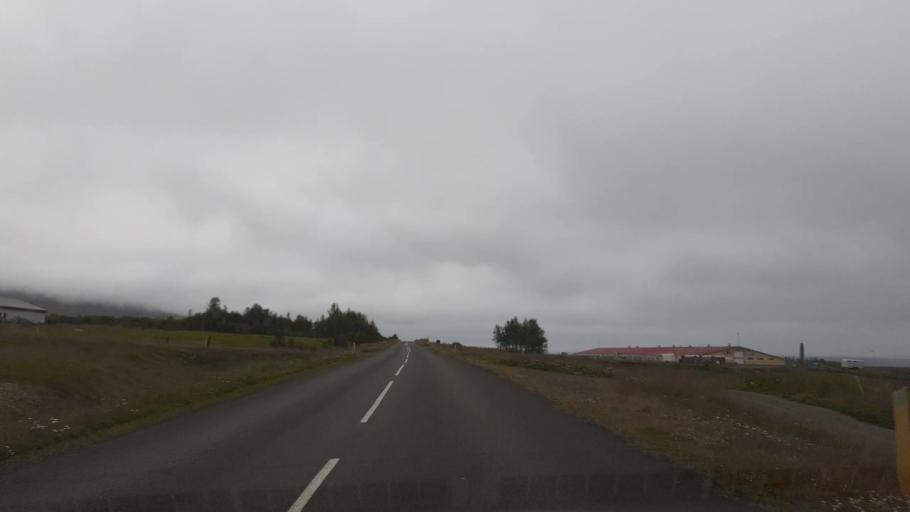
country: IS
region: Northeast
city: Dalvik
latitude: 65.9478
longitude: -18.5564
